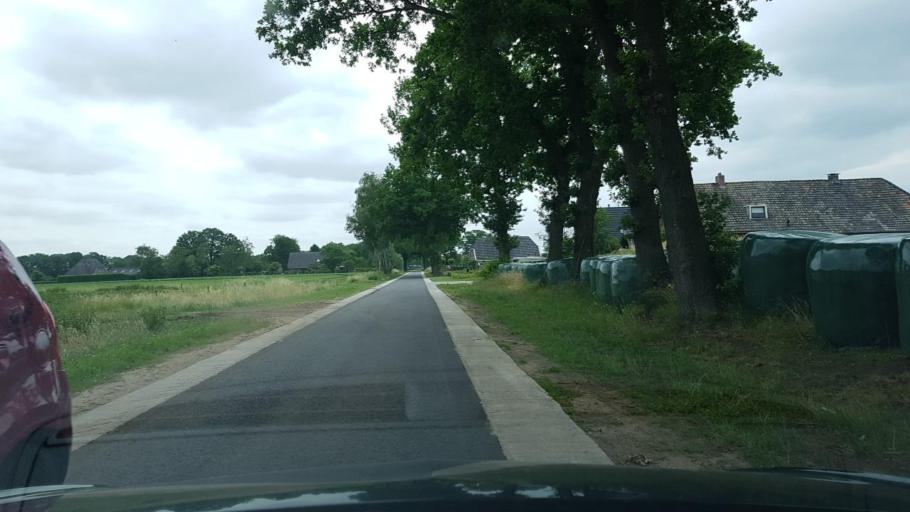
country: NL
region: Overijssel
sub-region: Gemeente Raalte
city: Raalte
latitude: 52.3480
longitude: 6.3728
